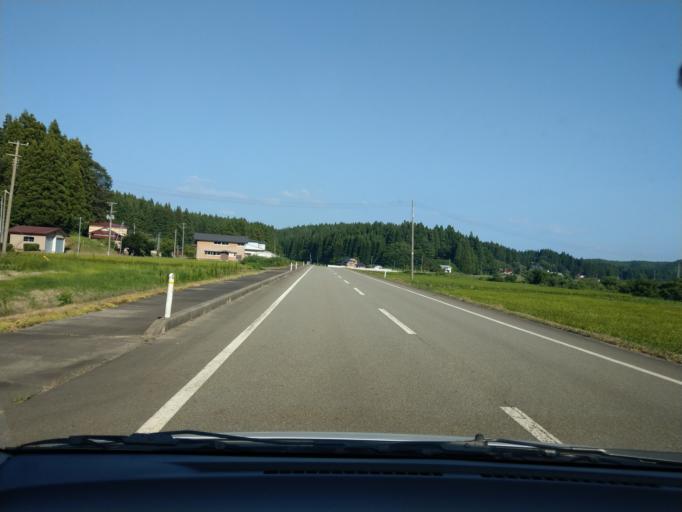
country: JP
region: Akita
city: Akita
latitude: 39.6033
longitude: 140.2248
